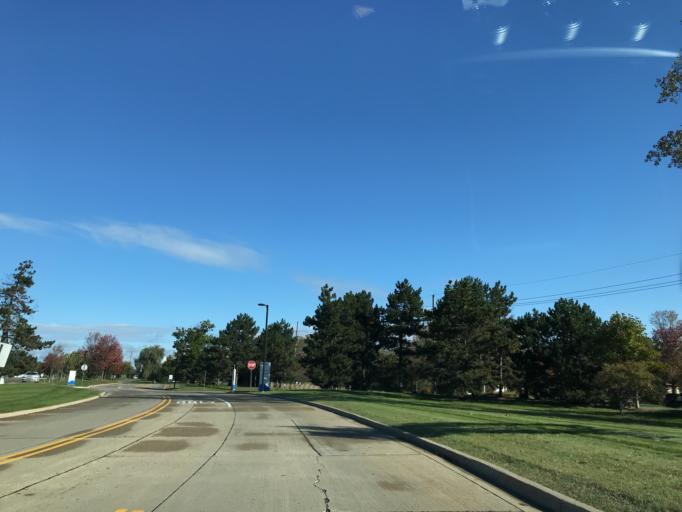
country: US
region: Michigan
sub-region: Oakland County
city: Novi
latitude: 42.4861
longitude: -83.5162
